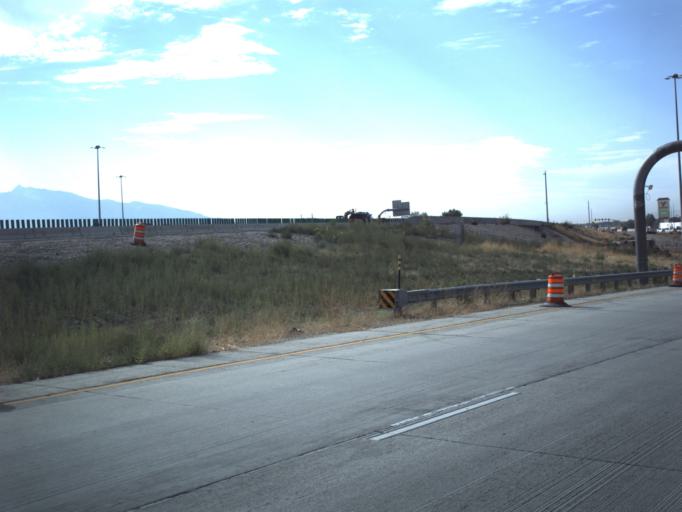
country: US
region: Utah
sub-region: Salt Lake County
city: Taylorsville
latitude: 40.6985
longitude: -111.9532
